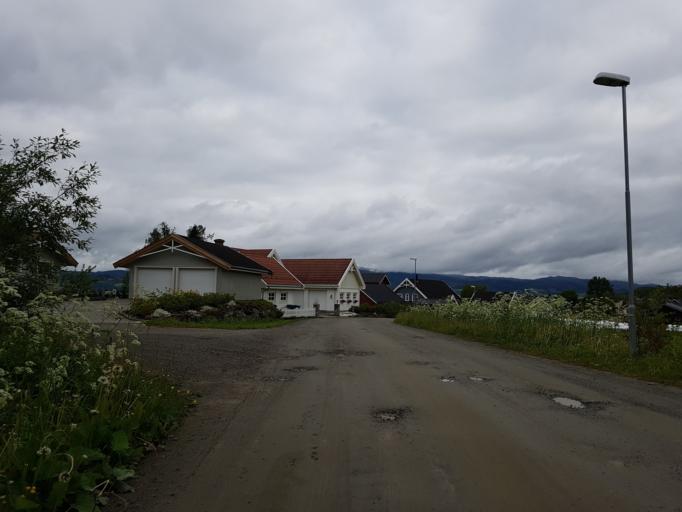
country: NO
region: Sor-Trondelag
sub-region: Selbu
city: Mebonden
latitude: 63.2216
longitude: 11.0293
